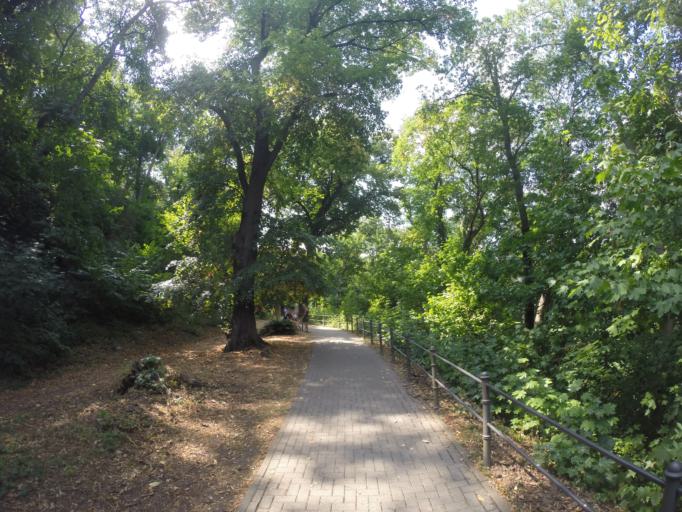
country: DE
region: Saxony-Anhalt
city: Wernigerode
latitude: 51.8317
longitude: 10.7949
